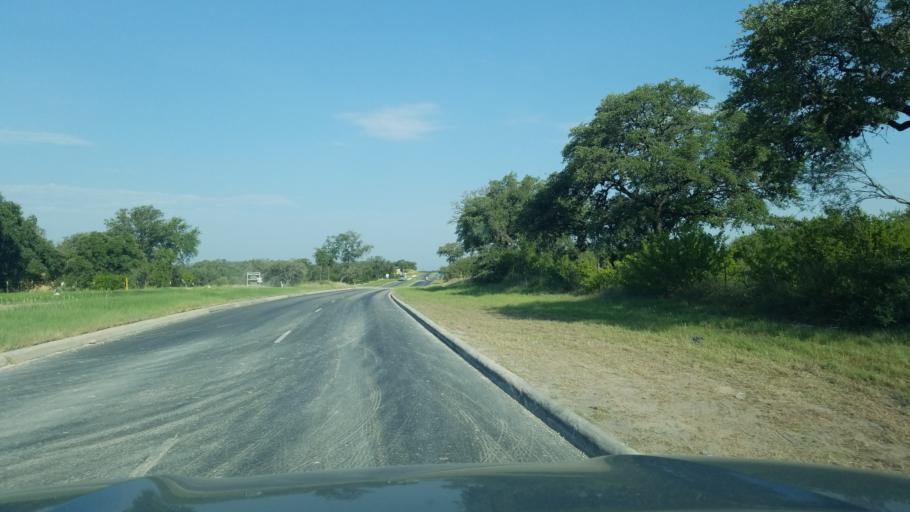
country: US
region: Texas
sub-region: Bexar County
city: Leon Valley
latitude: 29.4600
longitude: -98.7432
